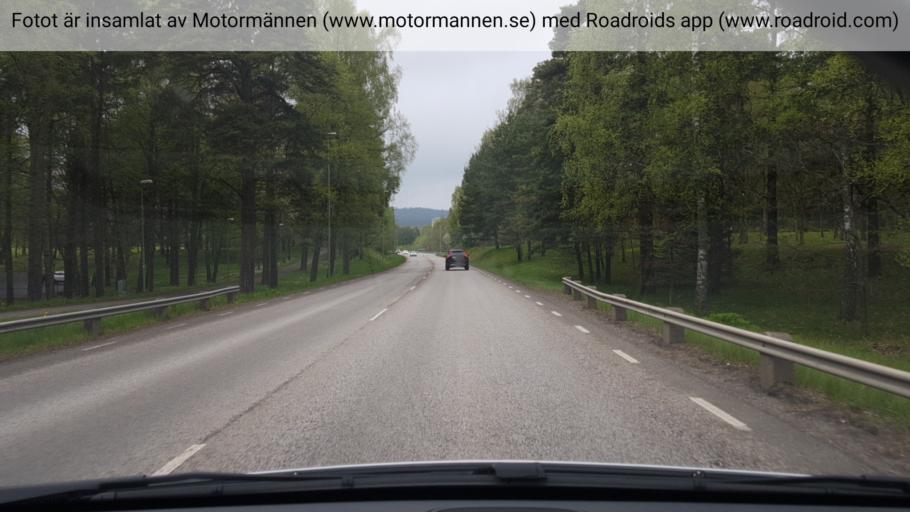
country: SE
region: Vaestra Goetaland
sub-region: Skovde Kommun
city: Skoevde
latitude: 58.4222
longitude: 13.8619
